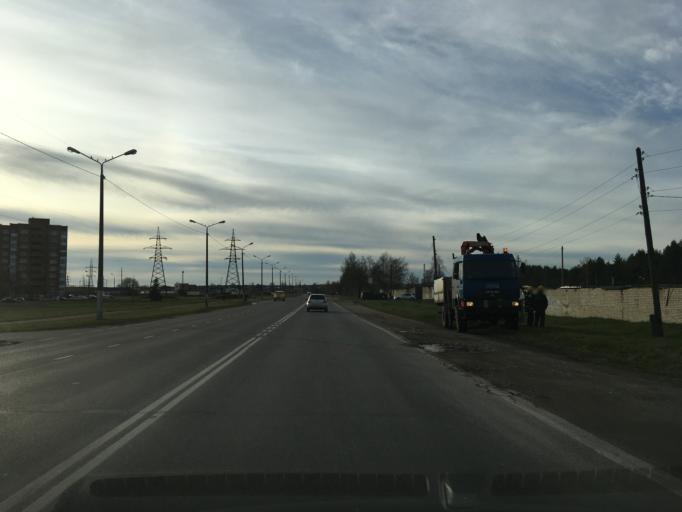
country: EE
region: Ida-Virumaa
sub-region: Narva linn
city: Narva
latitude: 59.3820
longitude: 28.1579
